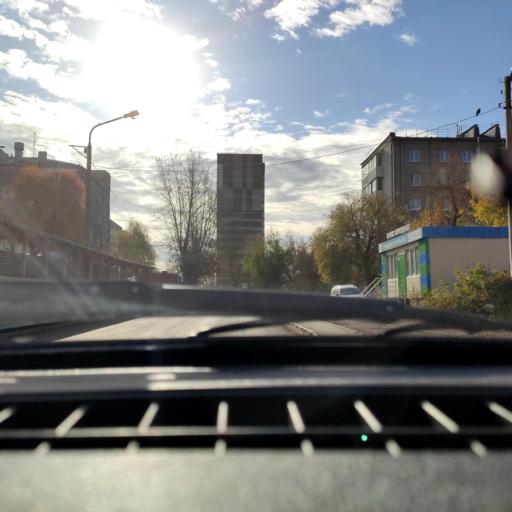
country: RU
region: Bashkortostan
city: Ufa
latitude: 54.8065
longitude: 56.1282
